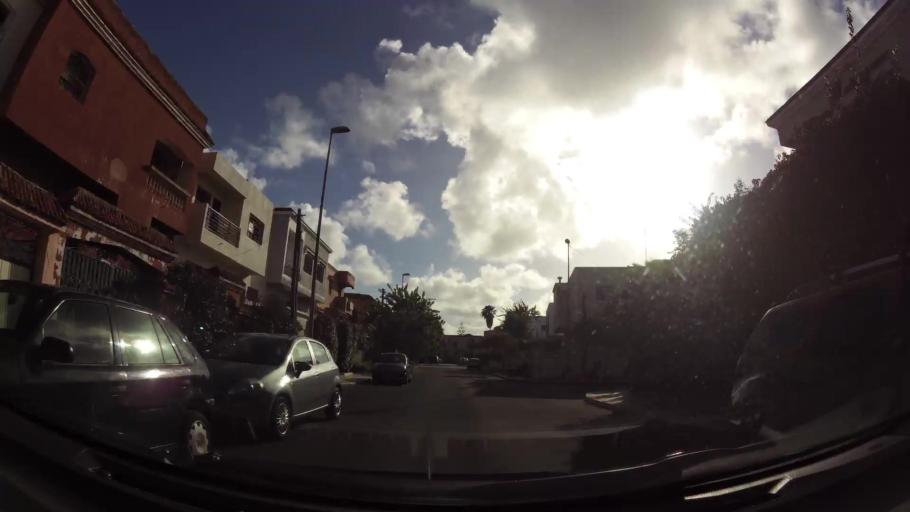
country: MA
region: Grand Casablanca
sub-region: Casablanca
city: Casablanca
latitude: 33.5731
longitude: -7.6869
